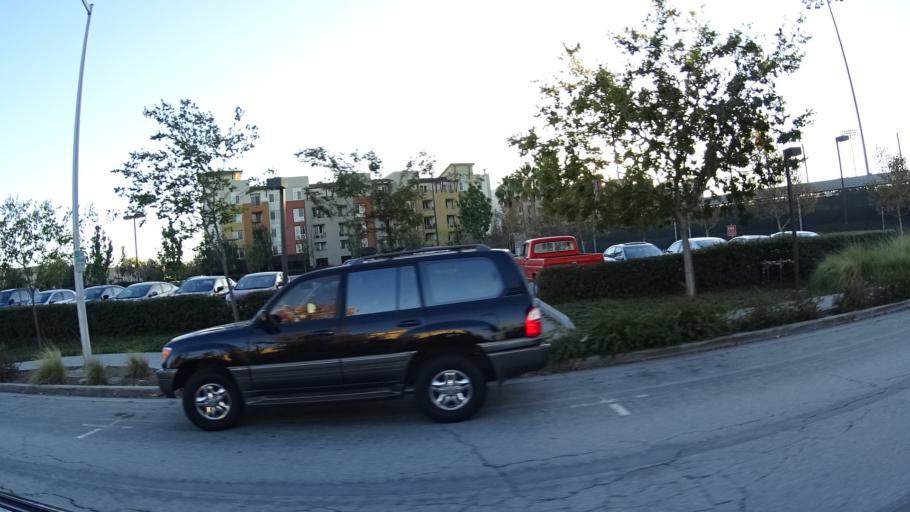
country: US
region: California
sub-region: Santa Clara County
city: Burbank
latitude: 37.3483
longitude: -121.9301
